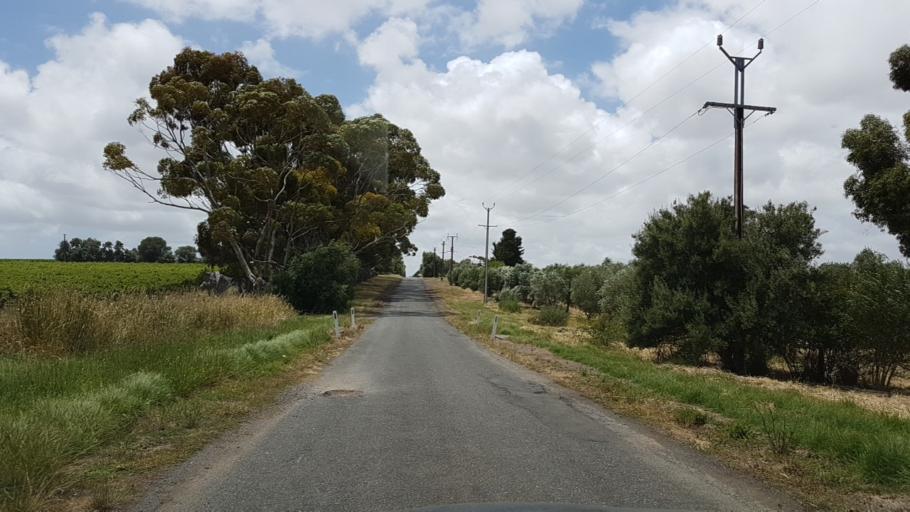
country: AU
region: South Australia
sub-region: Onkaparinga
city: McLaren Vale
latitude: -35.2406
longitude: 138.5404
